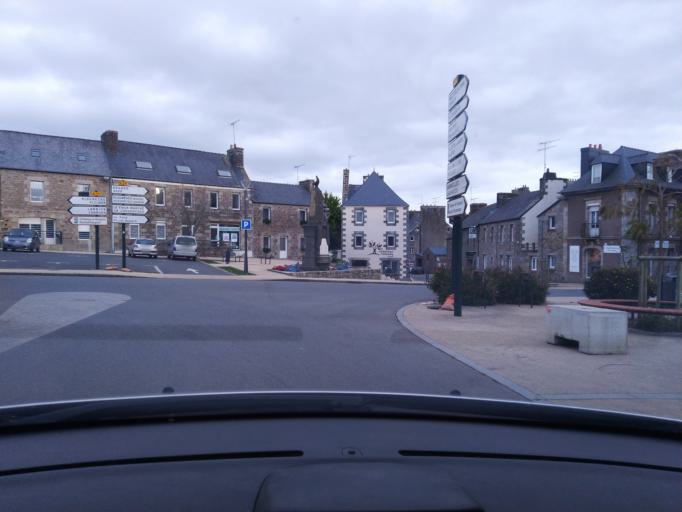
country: FR
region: Brittany
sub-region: Departement des Cotes-d'Armor
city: Plouaret
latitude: 48.6117
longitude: -3.4729
